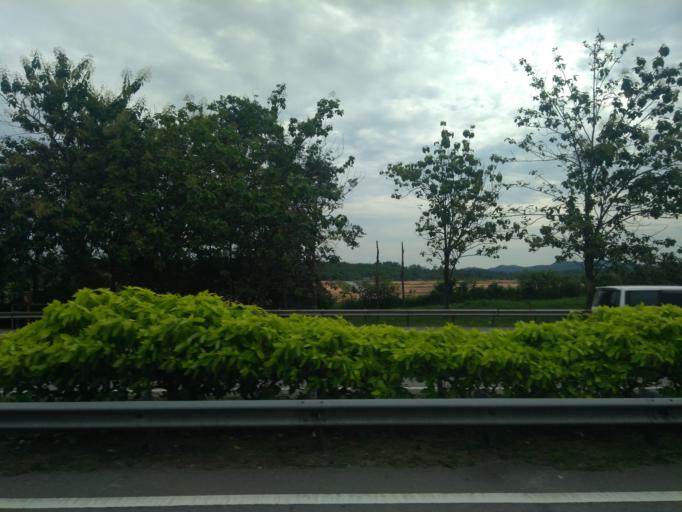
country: MY
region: Melaka
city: Pulau Sebang
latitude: 2.4364
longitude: 102.2027
